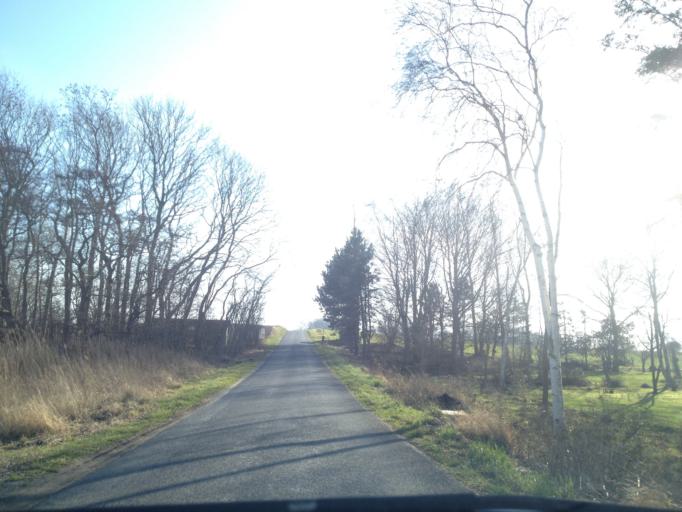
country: DK
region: South Denmark
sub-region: Kerteminde Kommune
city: Munkebo
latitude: 55.5670
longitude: 10.6122
